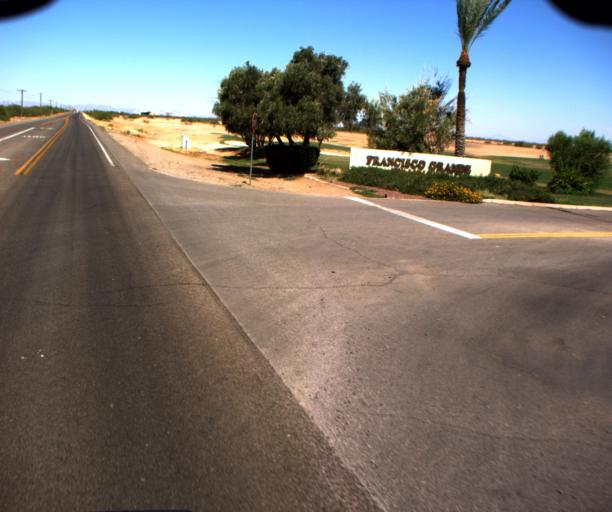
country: US
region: Arizona
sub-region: Pinal County
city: Casa Grande
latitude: 32.8795
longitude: -111.8484
